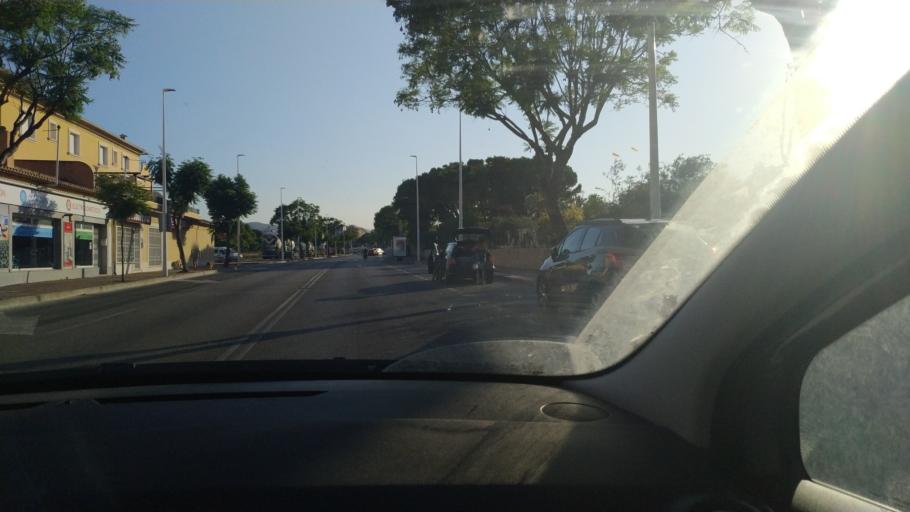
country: ES
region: Valencia
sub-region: Provincia de Alicante
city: Javea
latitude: 38.7886
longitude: 0.1703
